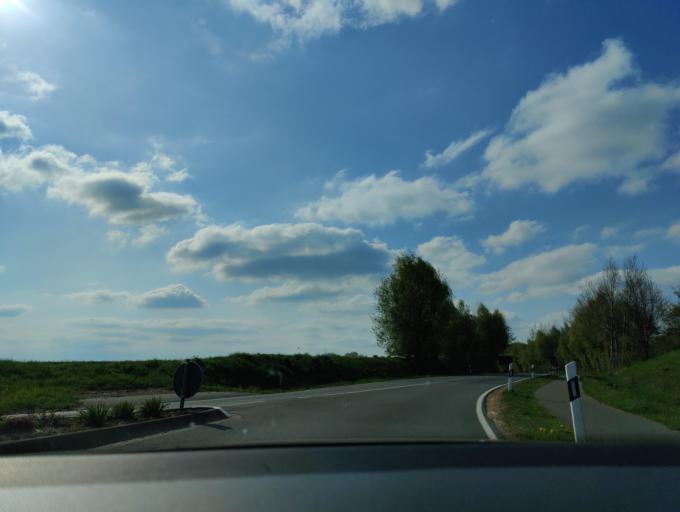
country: DE
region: Lower Saxony
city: Emsburen
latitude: 52.3855
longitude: 7.2875
